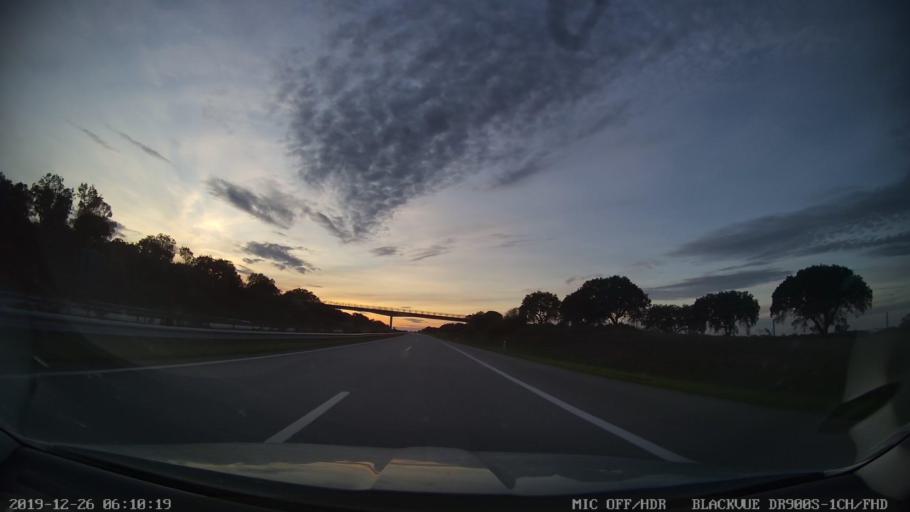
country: PT
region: Evora
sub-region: Montemor-O-Novo
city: Montemor-o-Novo
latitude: 38.6718
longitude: -8.1895
